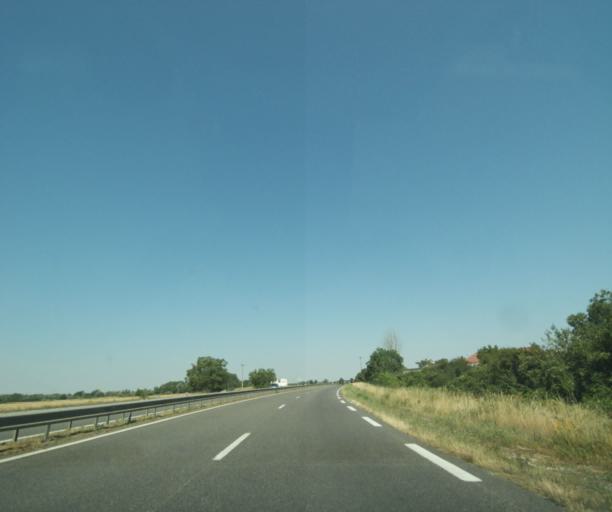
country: FR
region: Champagne-Ardenne
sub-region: Departement de la Haute-Marne
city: Villiers-en-Lieu
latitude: 48.6550
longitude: 4.8195
